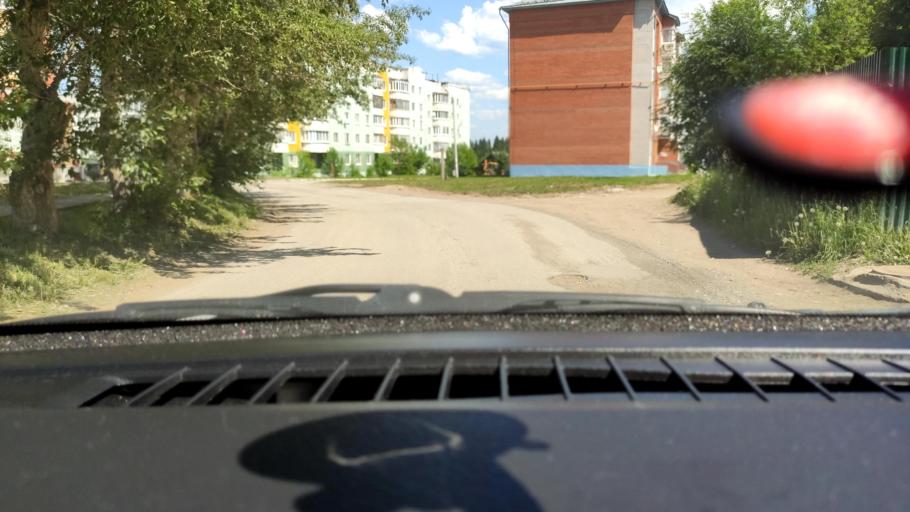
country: RU
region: Perm
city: Sylva
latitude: 58.0312
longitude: 56.7499
